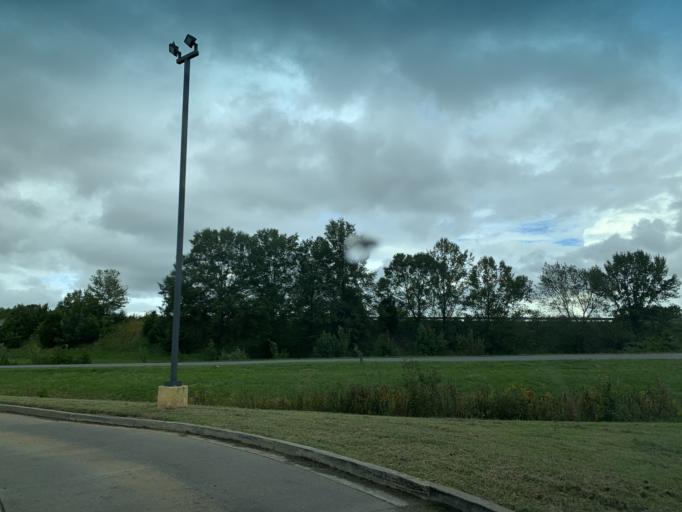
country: US
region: Maryland
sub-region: Caroline County
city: Denton
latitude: 38.8940
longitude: -75.8185
